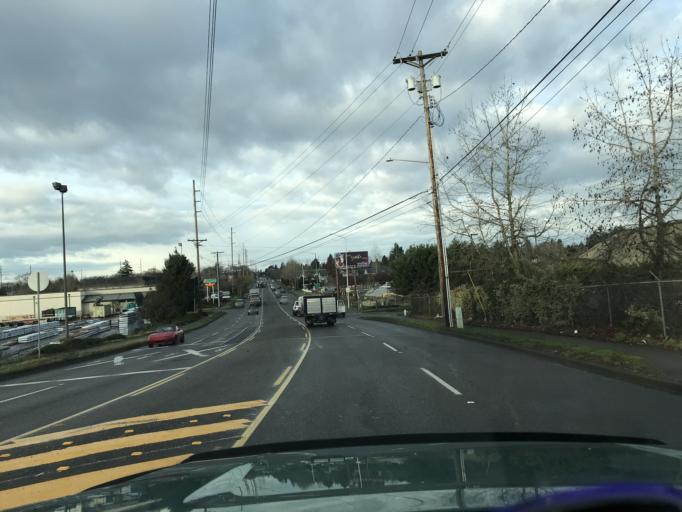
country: US
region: Washington
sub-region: Pierce County
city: Lakewood
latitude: 47.1905
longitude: -122.4857
